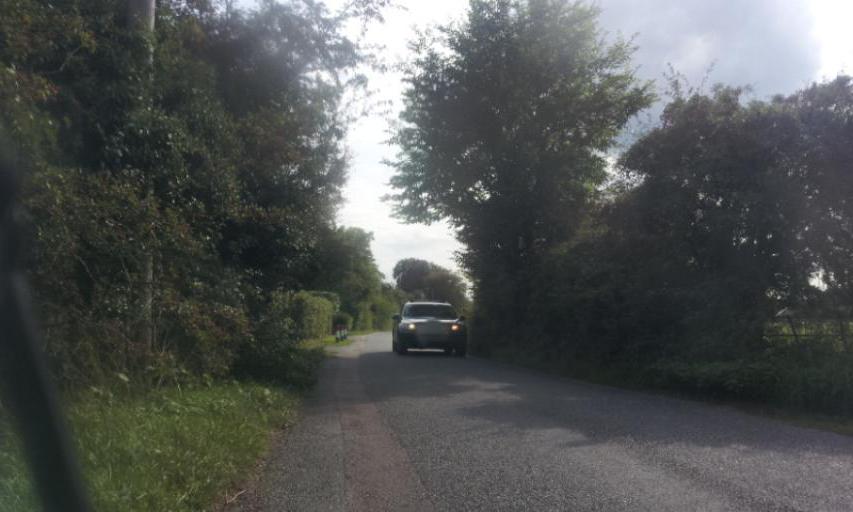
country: GB
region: England
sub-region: Kent
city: Hadlow
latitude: 51.2308
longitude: 0.3327
